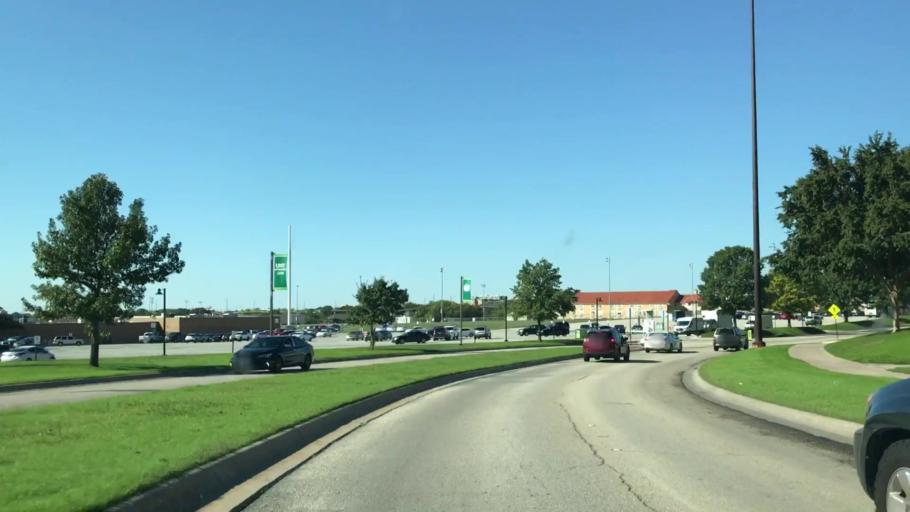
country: US
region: Texas
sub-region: Denton County
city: Denton
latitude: 33.2072
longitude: -97.1548
